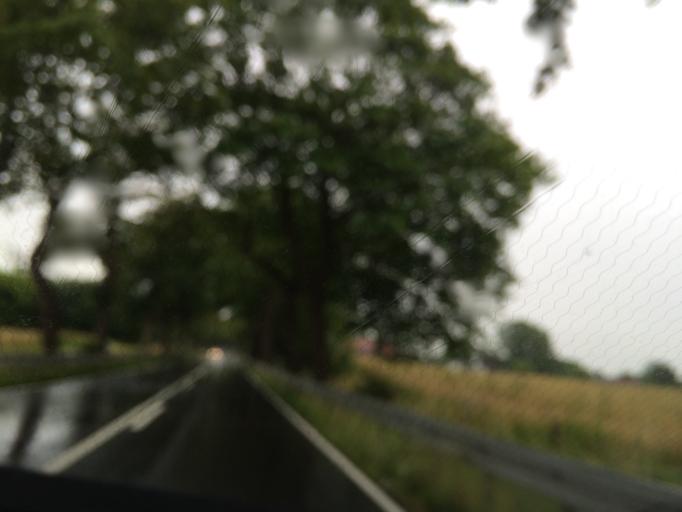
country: DE
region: Mecklenburg-Vorpommern
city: Kramerhof
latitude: 54.3474
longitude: 13.0466
